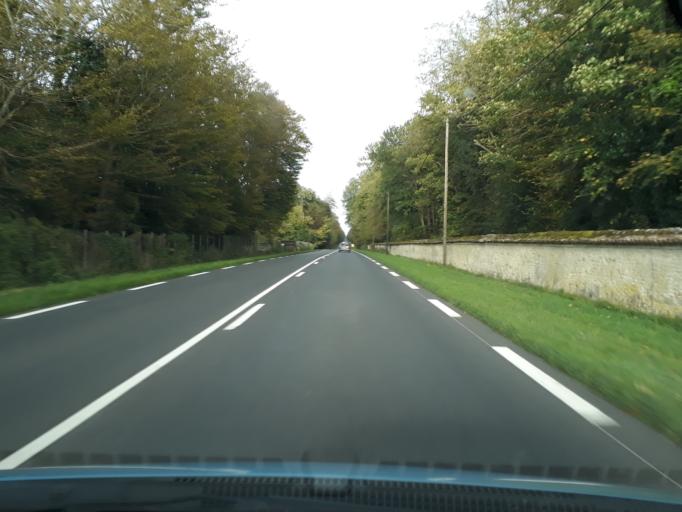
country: FR
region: Ile-de-France
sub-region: Departement de Seine-et-Marne
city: Acheres-la-Foret
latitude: 48.3505
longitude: 2.6119
